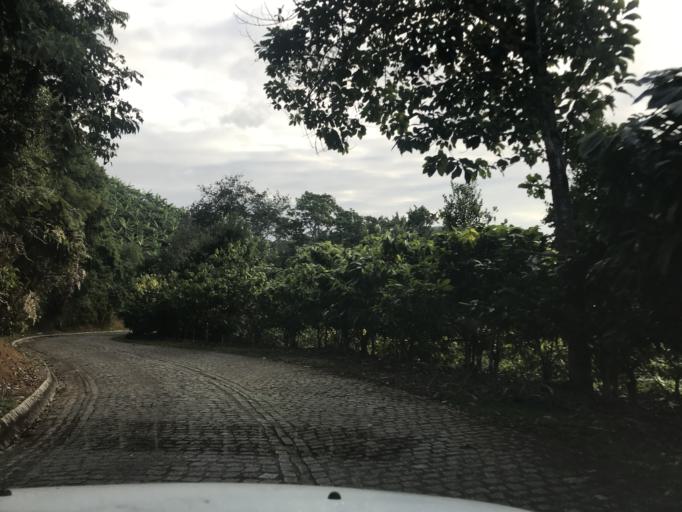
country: BR
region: Bahia
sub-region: Gandu
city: Gandu
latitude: -13.8986
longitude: -39.4745
